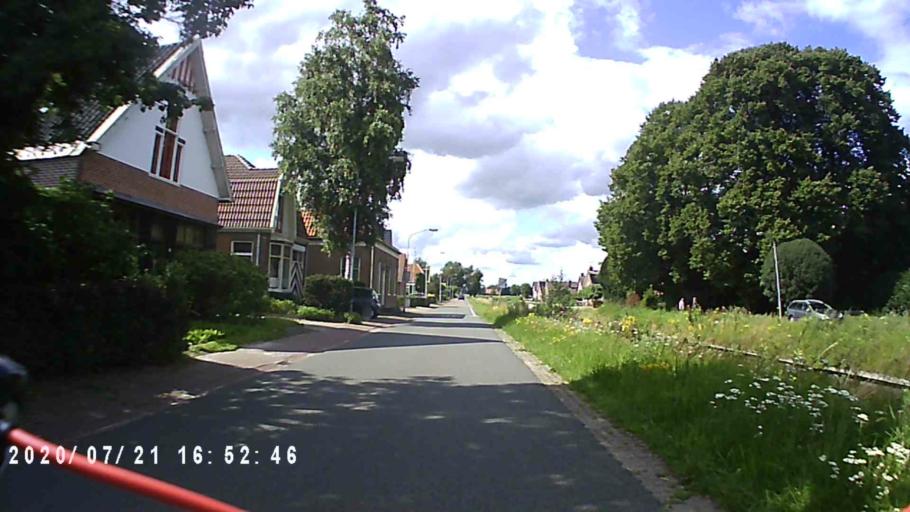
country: NL
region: Groningen
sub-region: Gemeente Hoogezand-Sappemeer
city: Hoogezand
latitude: 53.1236
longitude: 6.7711
